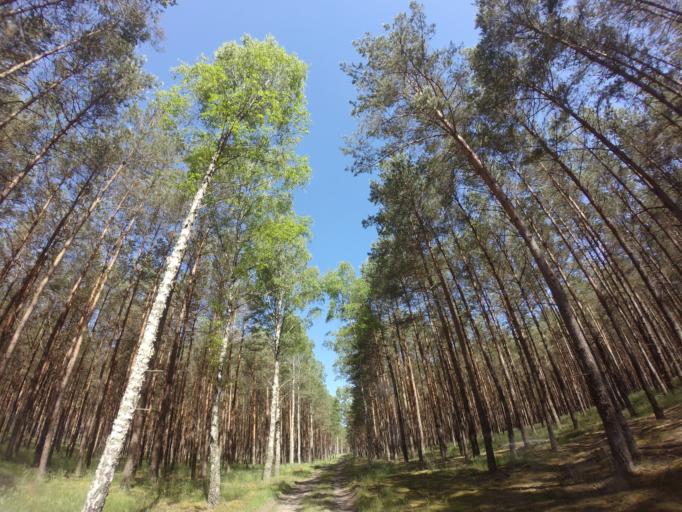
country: PL
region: West Pomeranian Voivodeship
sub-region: Powiat drawski
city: Kalisz Pomorski
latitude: 53.1822
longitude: 15.9827
